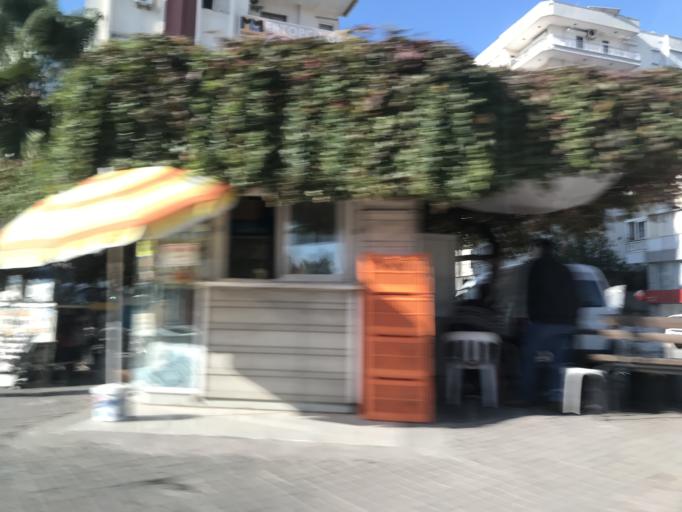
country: TR
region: Antalya
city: Antalya
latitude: 36.8956
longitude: 30.7071
